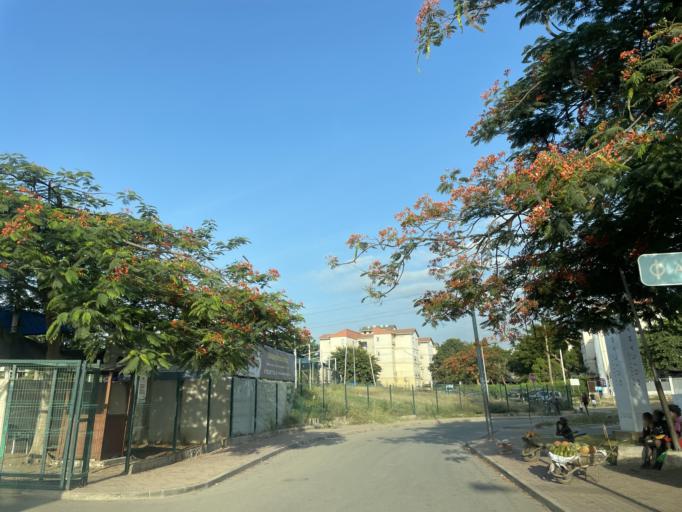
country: AO
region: Luanda
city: Luanda
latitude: -8.9046
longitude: 13.2353
